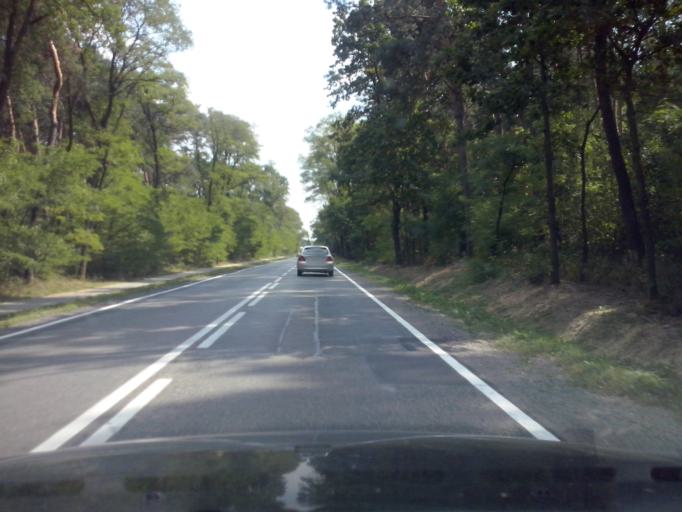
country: PL
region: Subcarpathian Voivodeship
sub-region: Powiat nizanski
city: Raclawice
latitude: 50.5065
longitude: 22.1748
